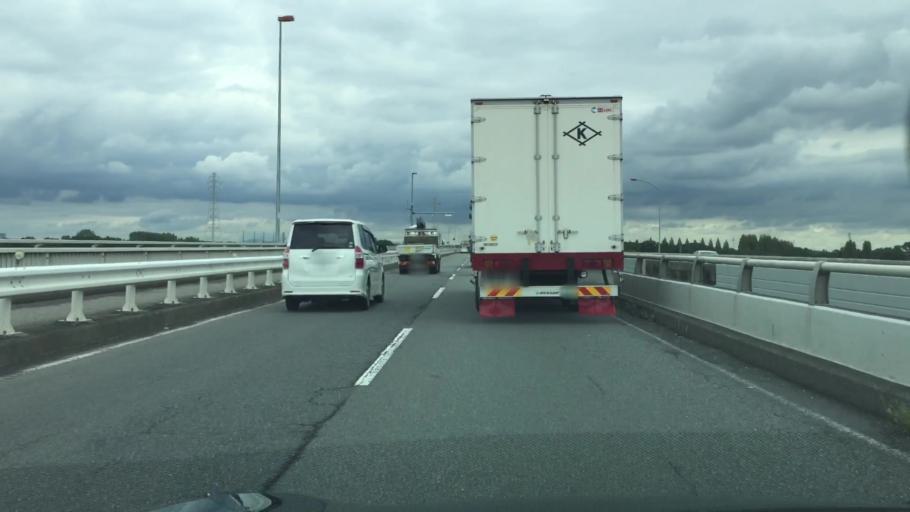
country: JP
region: Saitama
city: Kamifukuoka
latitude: 35.9141
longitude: 139.5428
